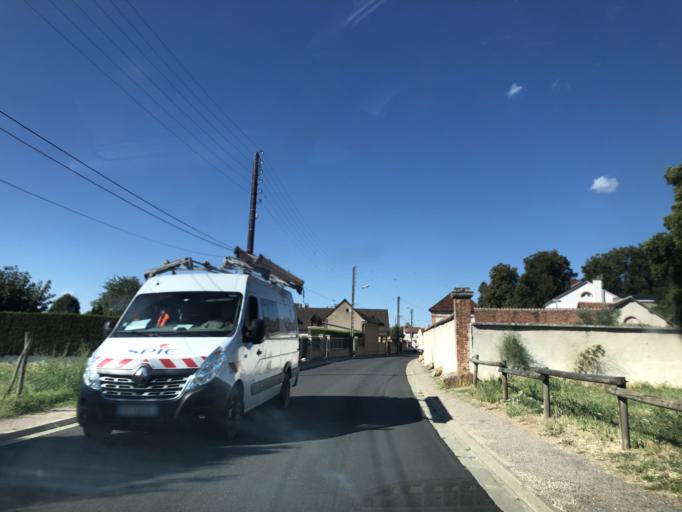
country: FR
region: Bourgogne
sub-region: Departement de l'Yonne
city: Appoigny
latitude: 47.8724
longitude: 3.5264
